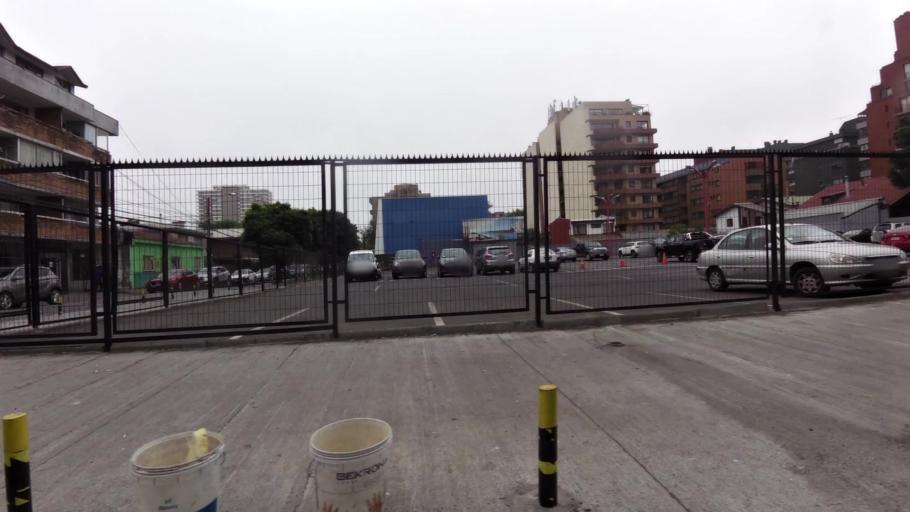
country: CL
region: Biobio
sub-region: Provincia de Concepcion
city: Concepcion
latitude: -36.8241
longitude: -73.0384
